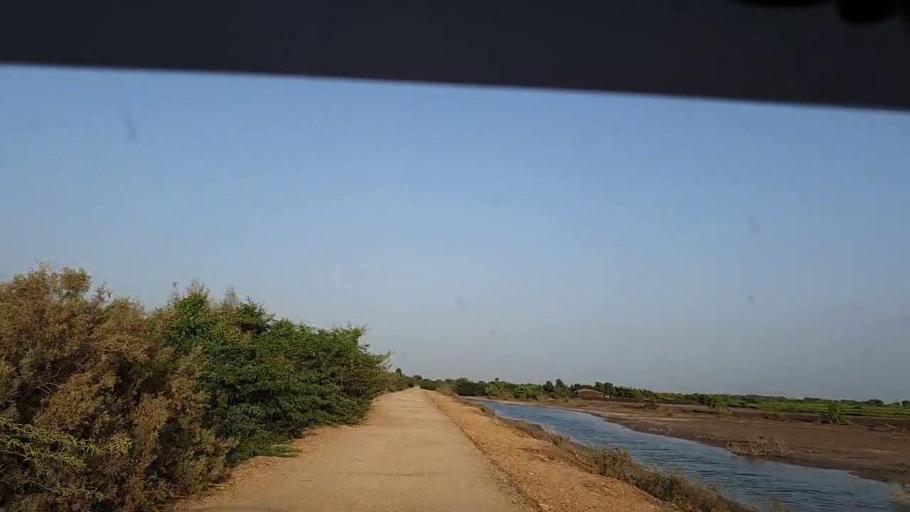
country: PK
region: Sindh
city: Kadhan
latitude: 24.5468
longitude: 68.9476
